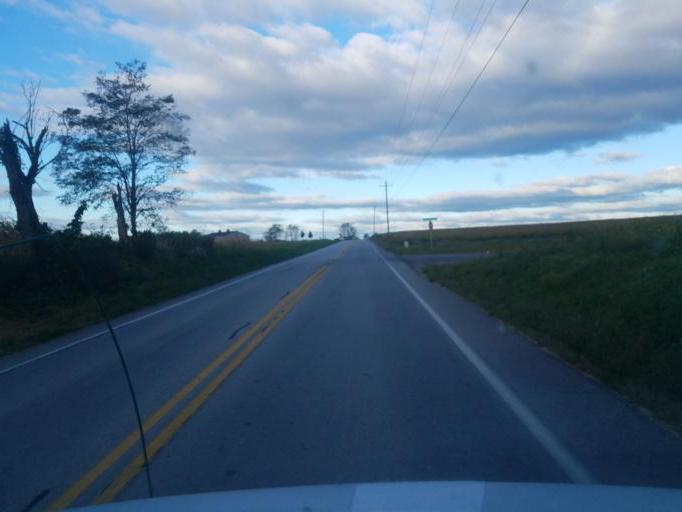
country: US
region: Pennsylvania
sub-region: Adams County
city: East Berlin
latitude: 39.9378
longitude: -77.0168
